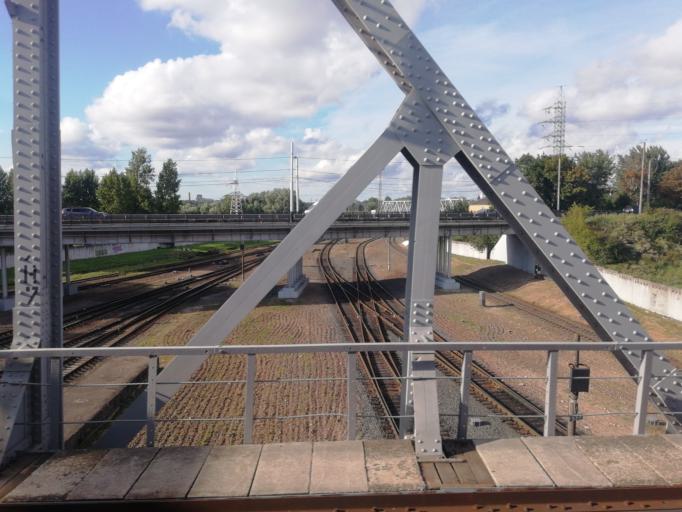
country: RU
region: Kaliningrad
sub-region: Gorod Kaliningrad
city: Kaliningrad
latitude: 54.6953
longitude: 20.4901
